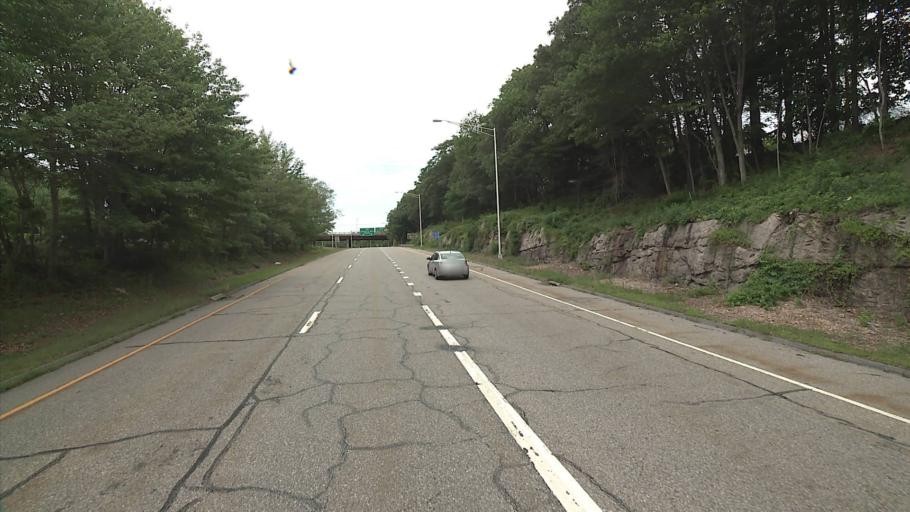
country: US
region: Connecticut
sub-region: New London County
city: Long Hill
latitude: 41.3602
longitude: -72.0609
